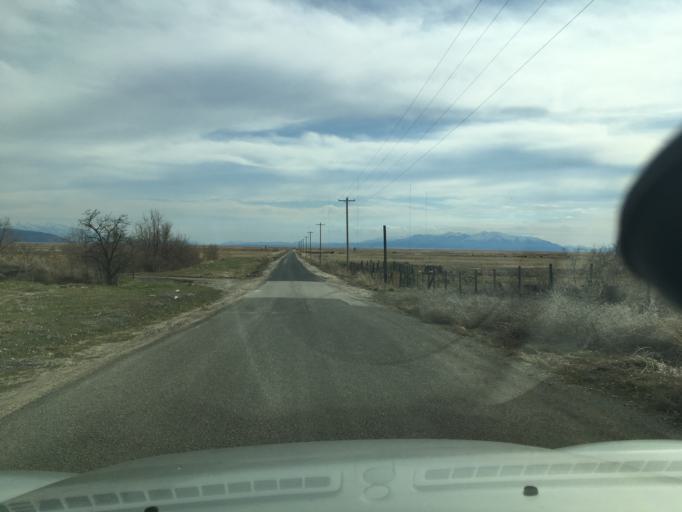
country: US
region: Utah
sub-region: Davis County
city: Syracuse
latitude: 41.0539
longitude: -112.0263
